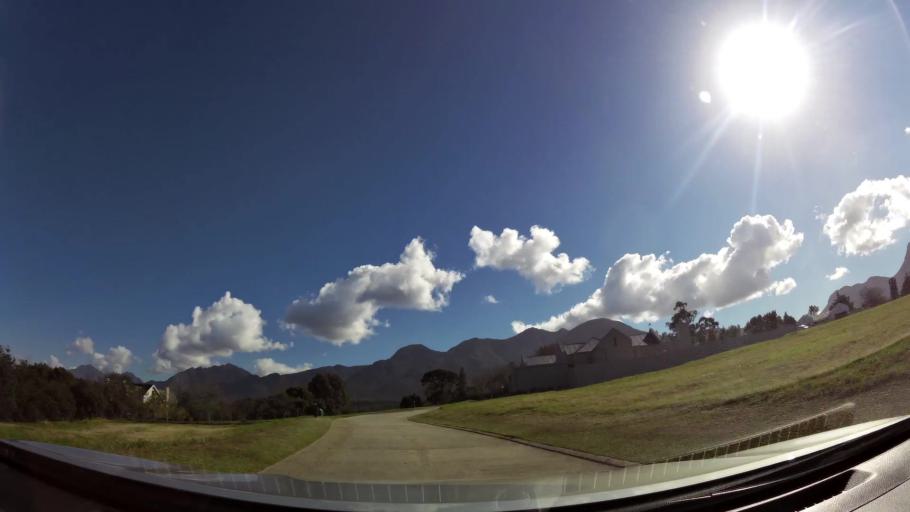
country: ZA
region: Western Cape
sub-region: Eden District Municipality
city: George
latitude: -33.9415
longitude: 22.4040
